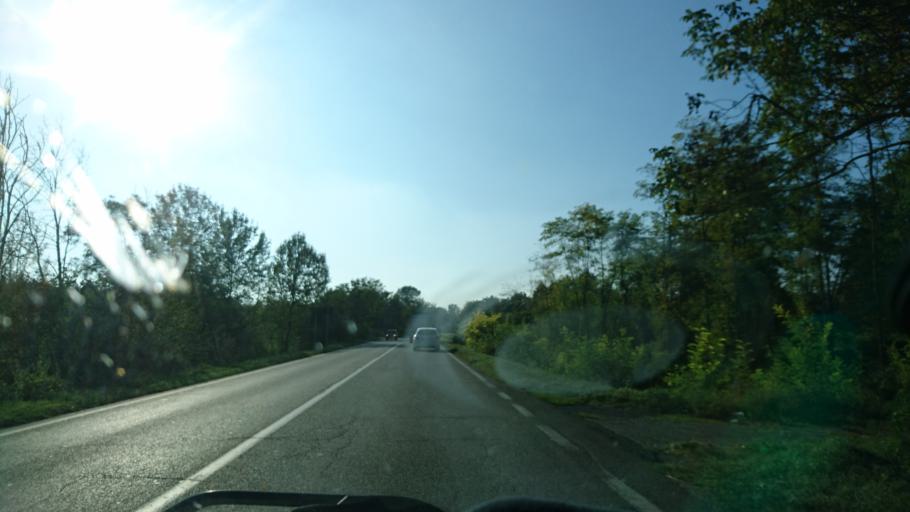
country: IT
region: Piedmont
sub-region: Provincia di Alessandria
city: Acqui Terme
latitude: 44.6675
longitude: 8.4629
